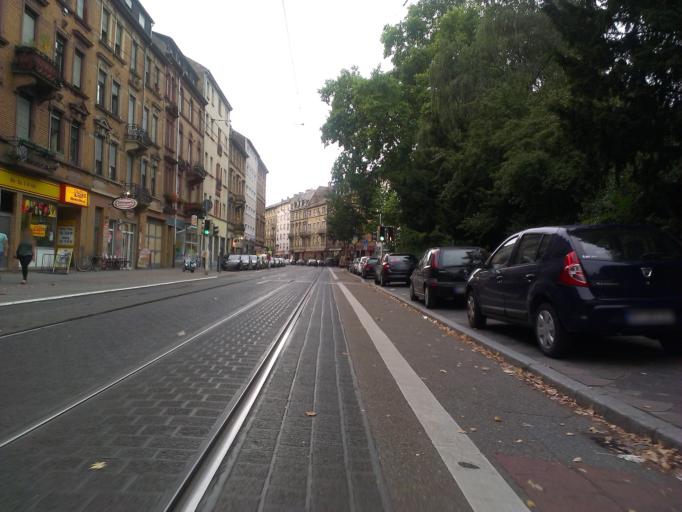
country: DE
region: Baden-Wuerttemberg
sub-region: Karlsruhe Region
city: Mannheim
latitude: 49.4790
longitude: 8.4818
